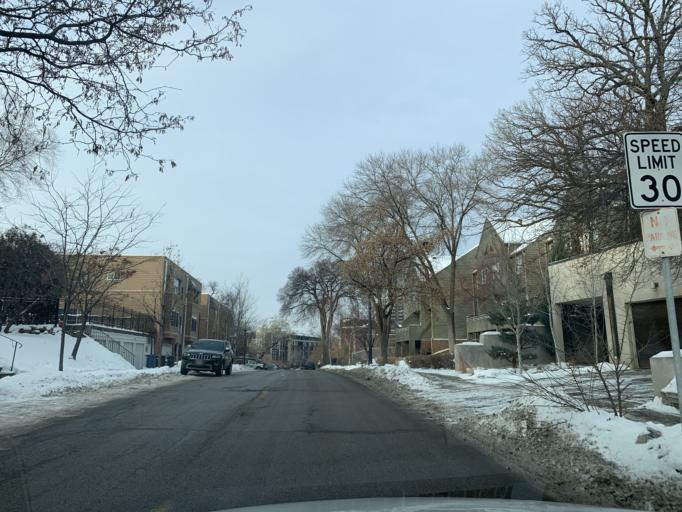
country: US
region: Minnesota
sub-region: Hennepin County
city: Minneapolis
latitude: 44.9643
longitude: -93.2809
